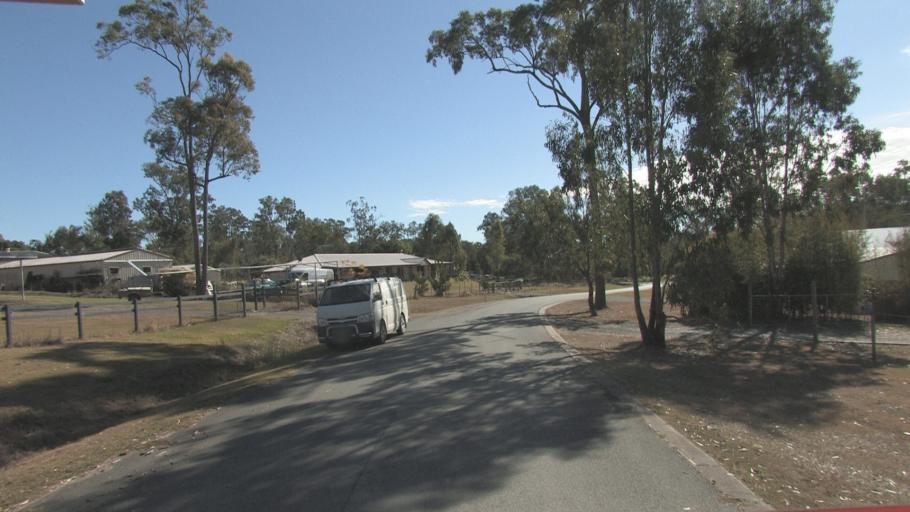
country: AU
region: Queensland
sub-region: Logan
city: North Maclean
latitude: -27.7995
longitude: 153.0444
